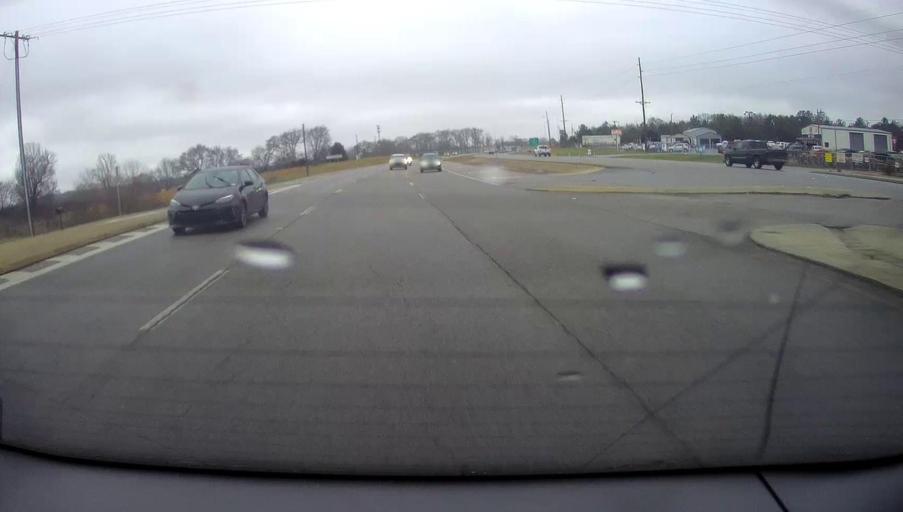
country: US
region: Alabama
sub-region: Morgan County
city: Decatur
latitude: 34.5916
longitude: -87.0305
